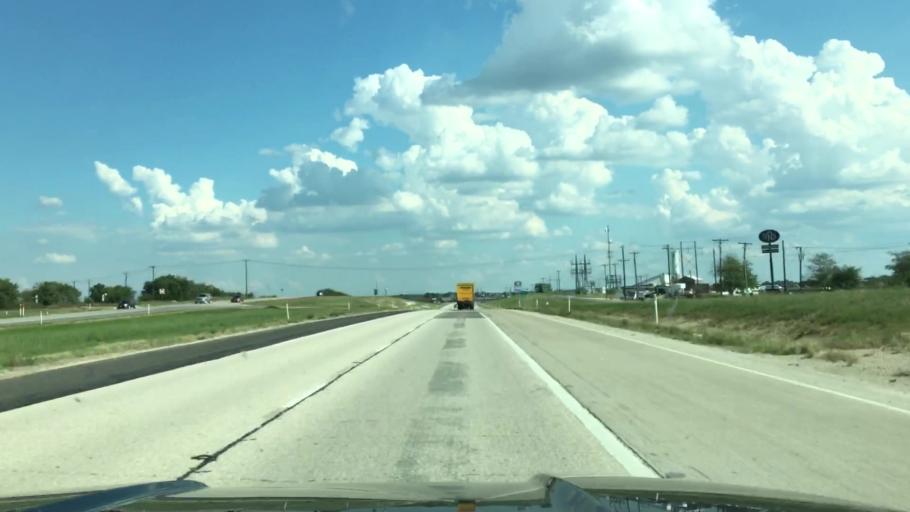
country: US
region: Texas
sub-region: Wise County
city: Decatur
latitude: 33.1812
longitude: -97.5488
